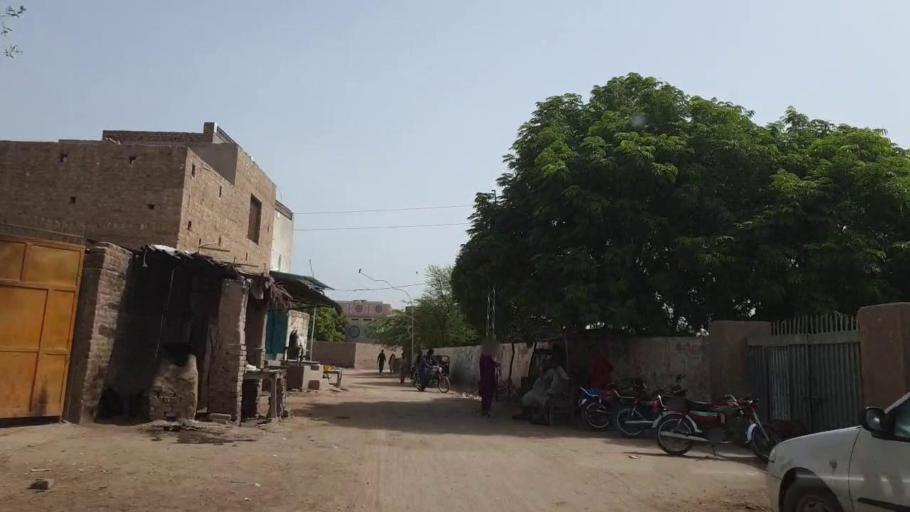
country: PK
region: Sindh
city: Sakrand
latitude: 26.1157
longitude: 68.3980
